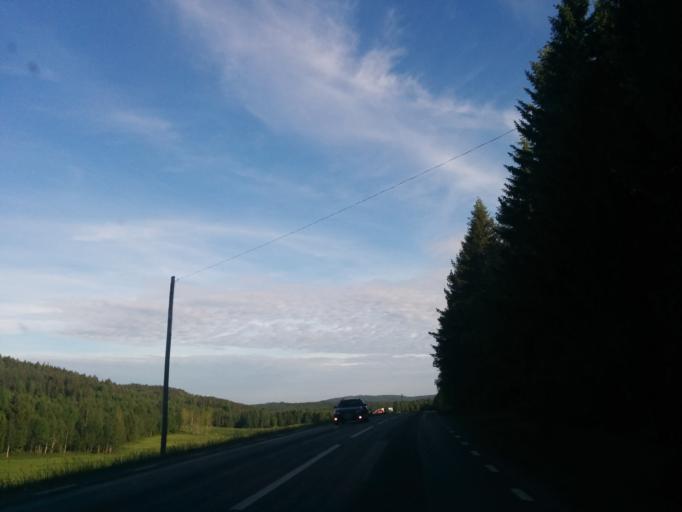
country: SE
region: Vaesternorrland
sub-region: Kramfors Kommun
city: Kramfors
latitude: 63.0114
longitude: 17.8313
